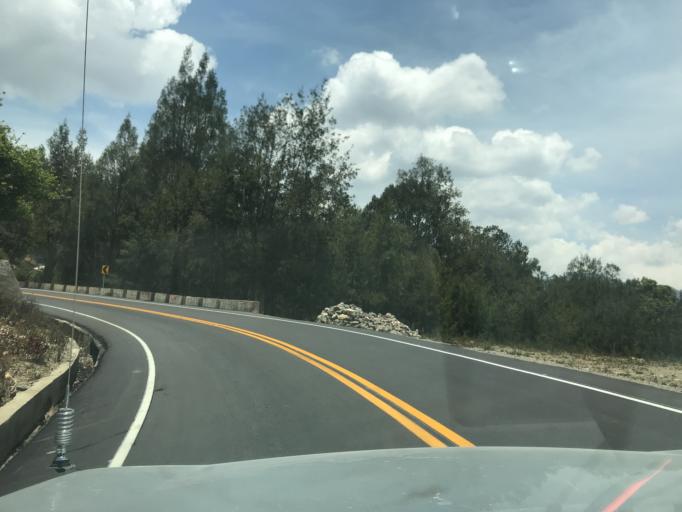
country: TL
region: Manufahi
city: Same
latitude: -8.8748
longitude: 125.5922
